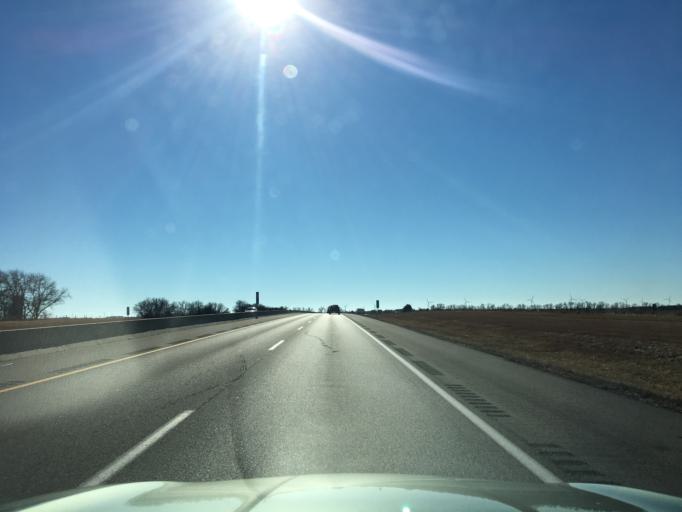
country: US
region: Kansas
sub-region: Sumner County
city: Wellington
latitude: 37.2019
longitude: -97.3401
